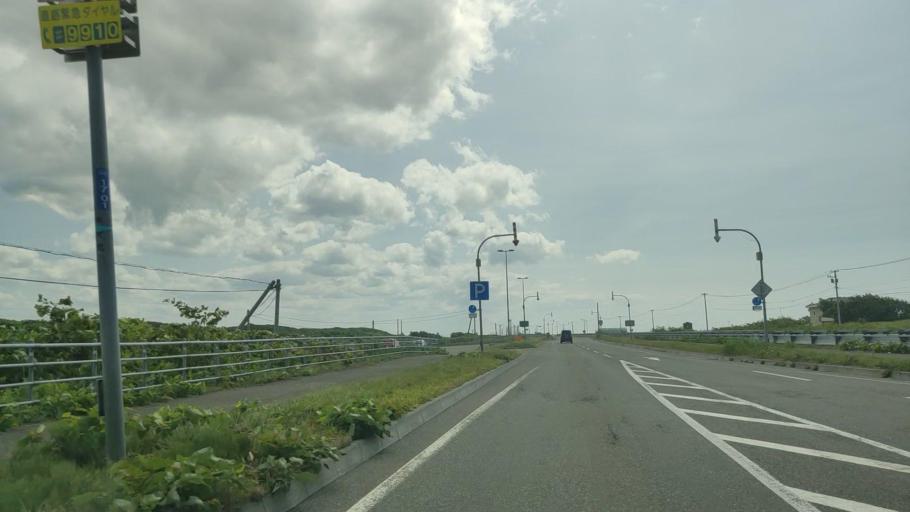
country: JP
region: Hokkaido
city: Makubetsu
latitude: 44.8721
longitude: 141.7518
